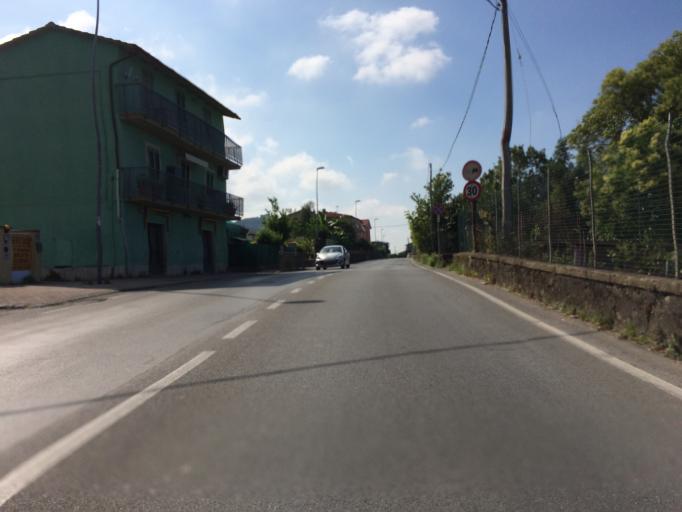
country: IT
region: Tuscany
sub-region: Provincia di Massa-Carrara
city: San Vito-Cerreto
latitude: 44.0214
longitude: 10.1488
